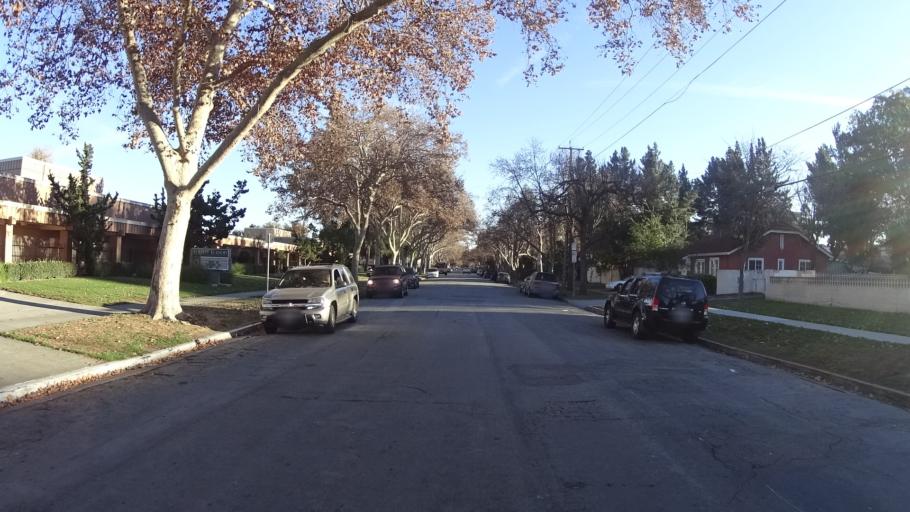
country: US
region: California
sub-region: Santa Clara County
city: San Jose
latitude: 37.3529
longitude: -121.9017
